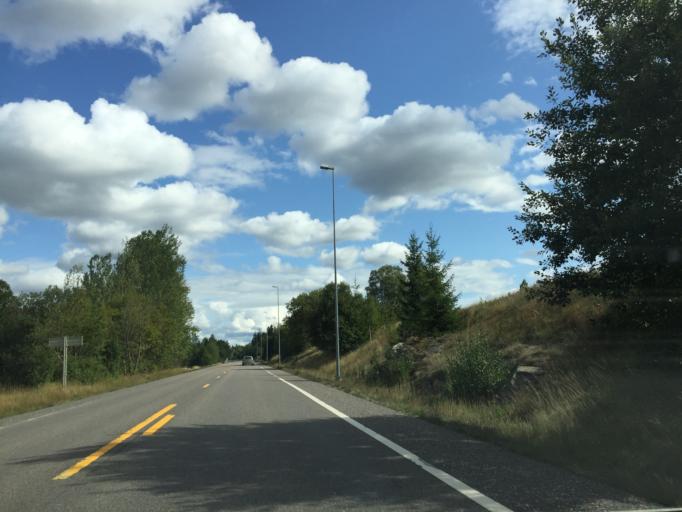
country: NO
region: Ostfold
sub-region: Hobol
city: Knappstad
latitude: 59.6191
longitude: 11.0282
